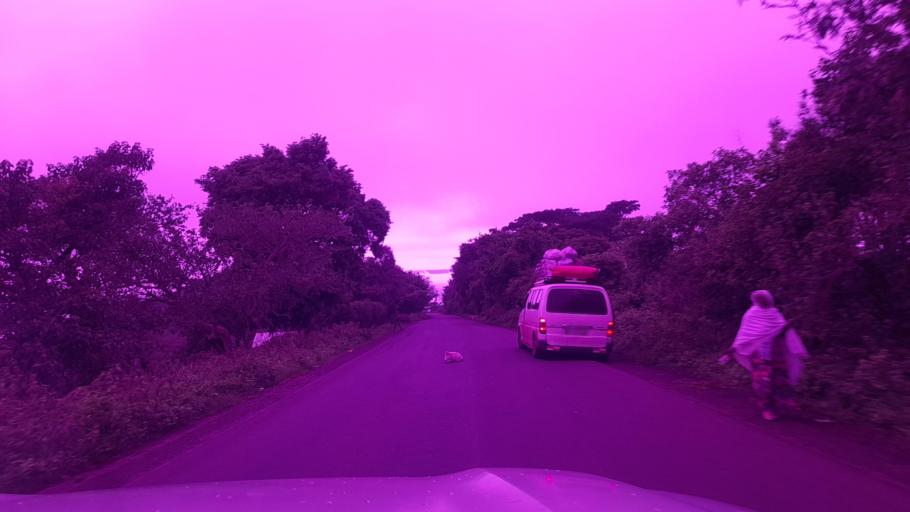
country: ET
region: Oromiya
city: Waliso
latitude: 8.1724
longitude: 37.5783
